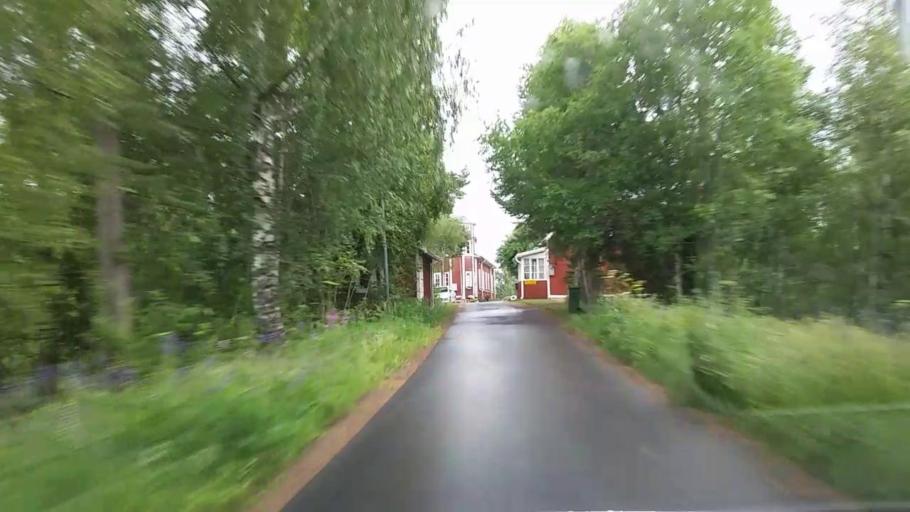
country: SE
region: Gaevleborg
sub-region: Ljusdals Kommun
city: Jaervsoe
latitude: 61.7153
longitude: 16.1774
